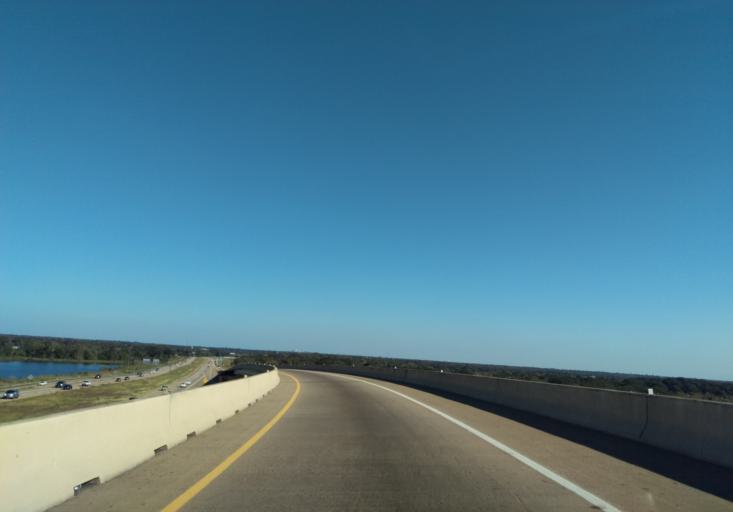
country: US
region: Texas
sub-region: Waller County
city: Hempstead
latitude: 30.1139
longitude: -96.0743
